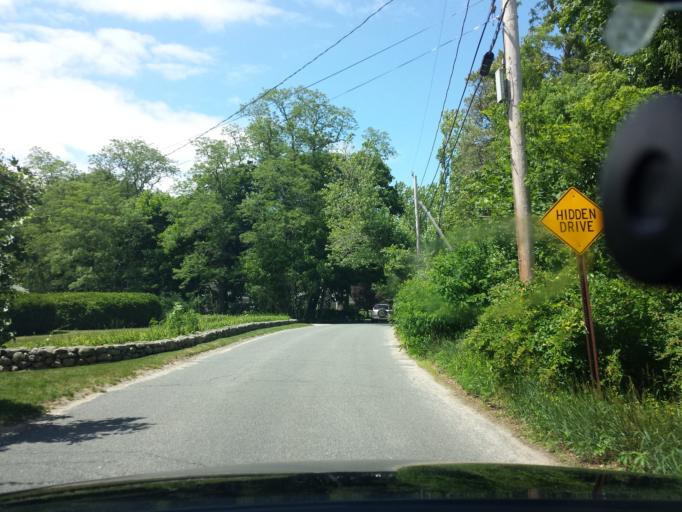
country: US
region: Massachusetts
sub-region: Barnstable County
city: Marstons Mills
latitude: 41.6487
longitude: -70.4138
